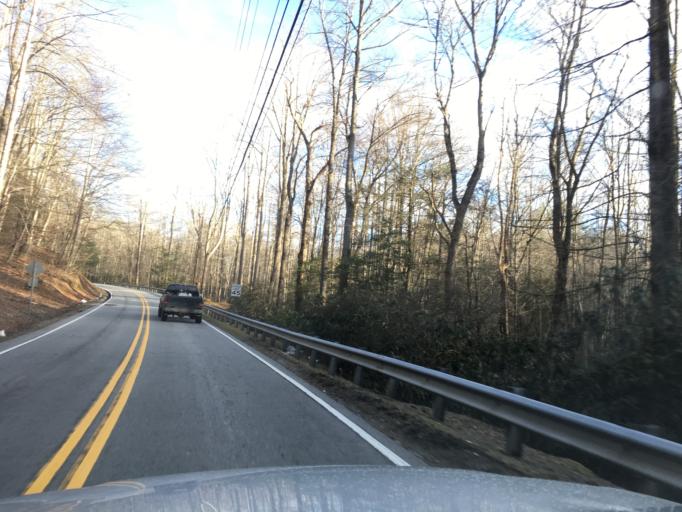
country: US
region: North Carolina
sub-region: Jackson County
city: Cullowhee
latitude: 35.1187
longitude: -83.0046
